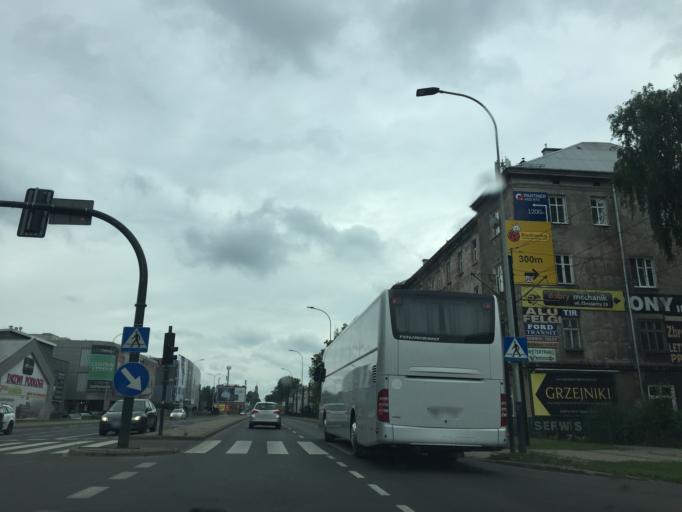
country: PL
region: Lesser Poland Voivodeship
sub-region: Krakow
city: Krakow
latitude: 50.0186
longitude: 19.9310
